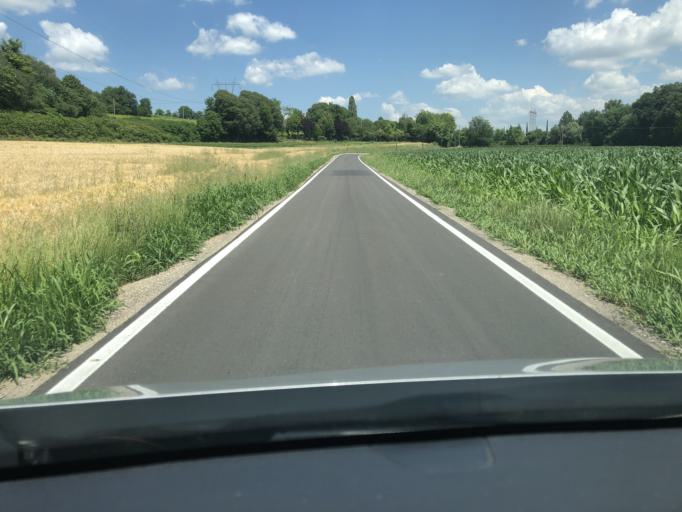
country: IT
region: Veneto
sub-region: Provincia di Verona
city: Rosegaferro
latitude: 45.3714
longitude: 10.8020
